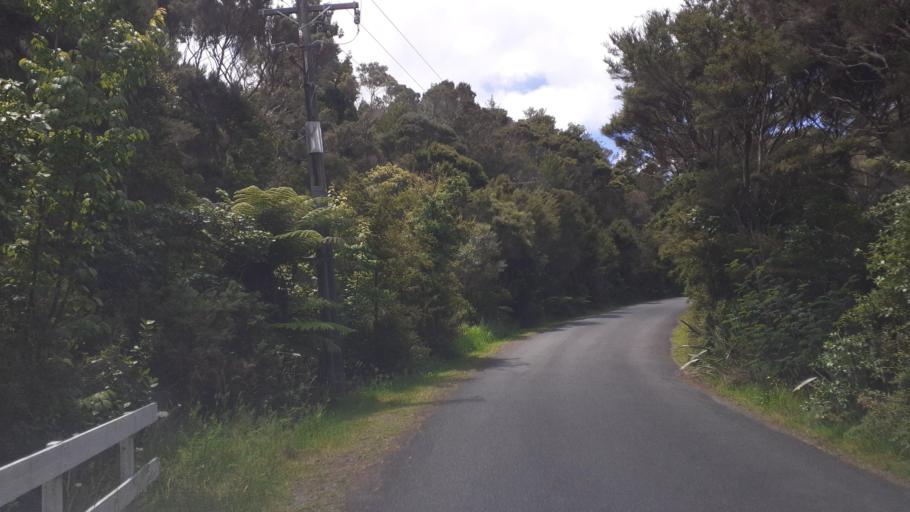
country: NZ
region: Northland
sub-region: Far North District
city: Paihia
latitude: -35.3121
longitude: 174.1130
